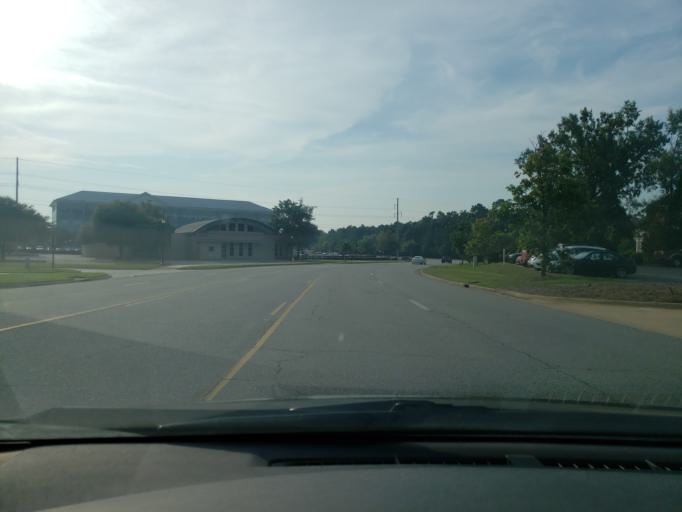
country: US
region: Georgia
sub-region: Dougherty County
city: Albany
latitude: 31.6106
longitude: -84.2206
